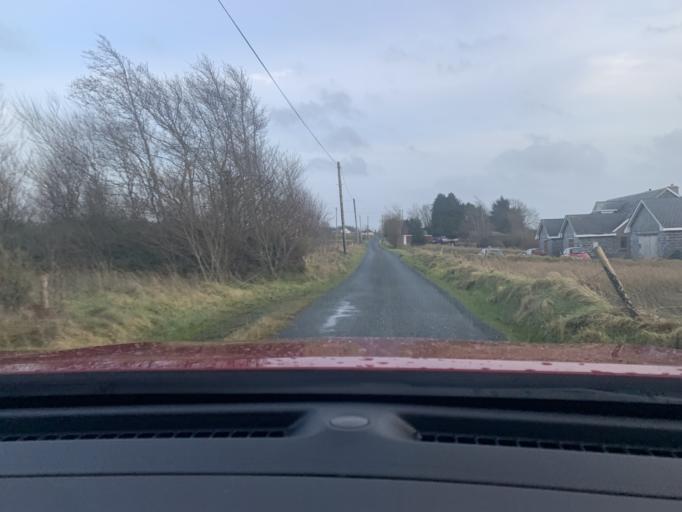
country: IE
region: Connaught
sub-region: Roscommon
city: Ballaghaderreen
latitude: 53.9547
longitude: -8.5282
